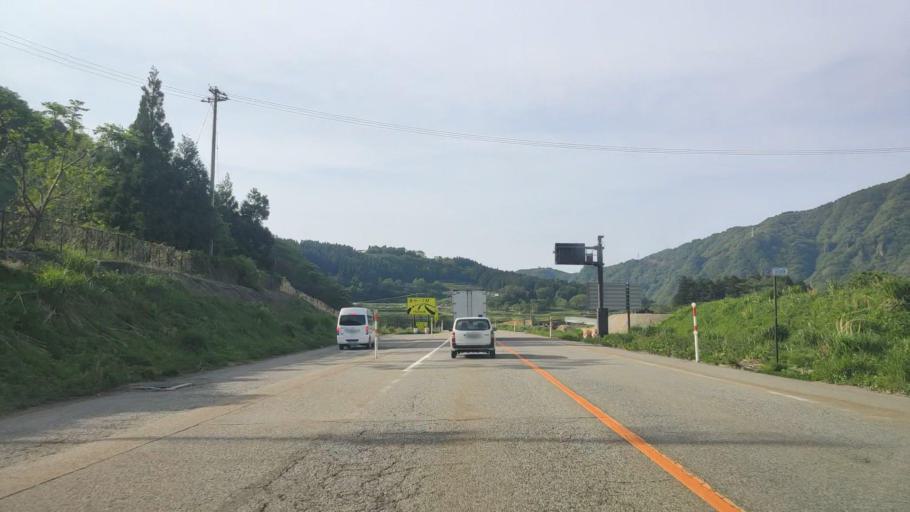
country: JP
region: Toyama
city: Yatsuomachi-higashikumisaka
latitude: 36.5320
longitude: 137.2261
